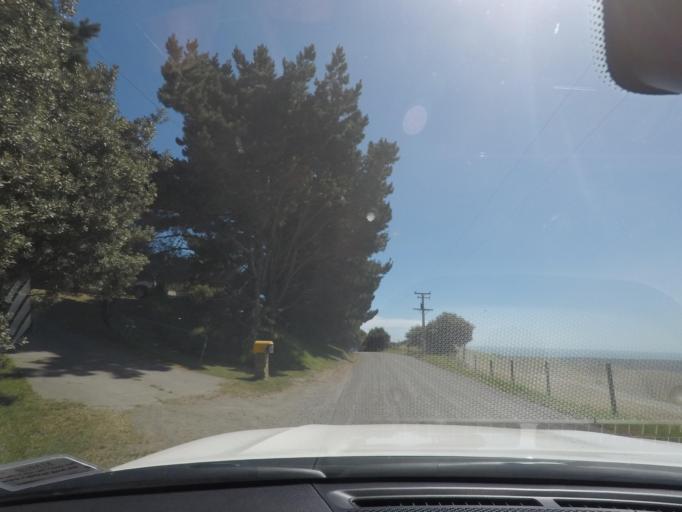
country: NZ
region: Auckland
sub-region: Auckland
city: Parakai
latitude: -36.5859
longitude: 174.2880
